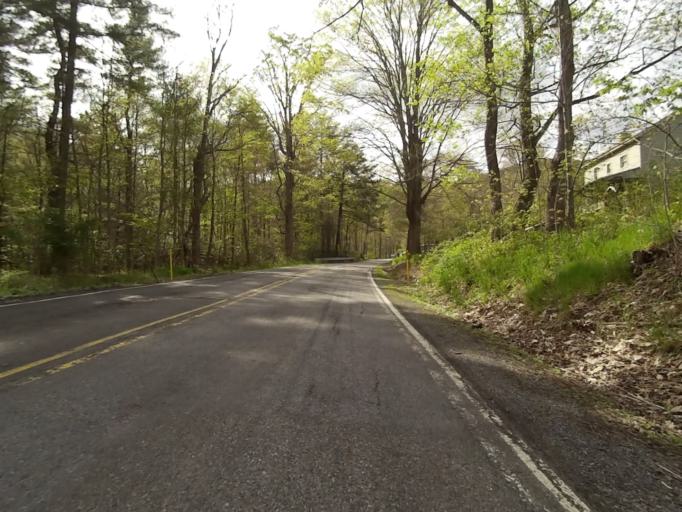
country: US
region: Pennsylvania
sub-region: Centre County
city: Park Forest Village
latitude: 40.8863
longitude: -77.9750
